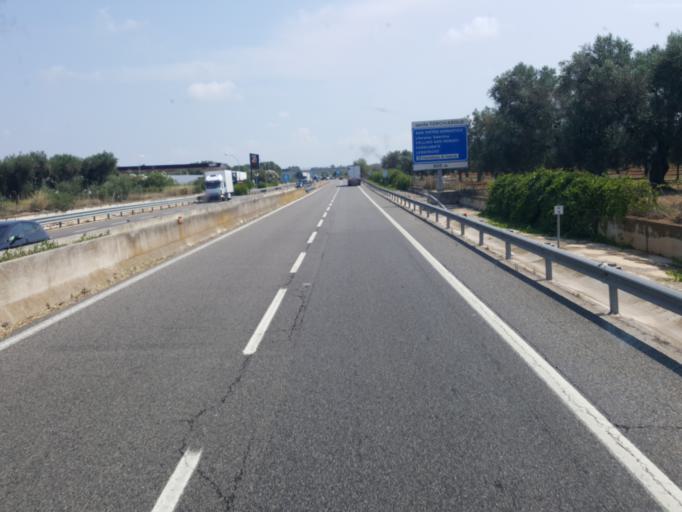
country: IT
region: Apulia
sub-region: Provincia di Brindisi
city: Torchiarolo
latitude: 40.4922
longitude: 18.0373
